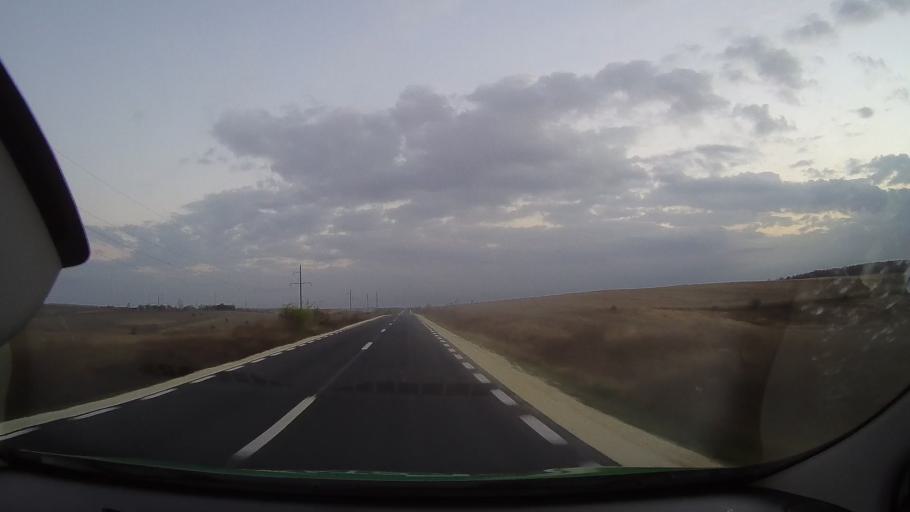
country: RO
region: Constanta
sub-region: Comuna Baneasa
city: Baneasa
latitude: 44.0868
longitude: 27.6879
